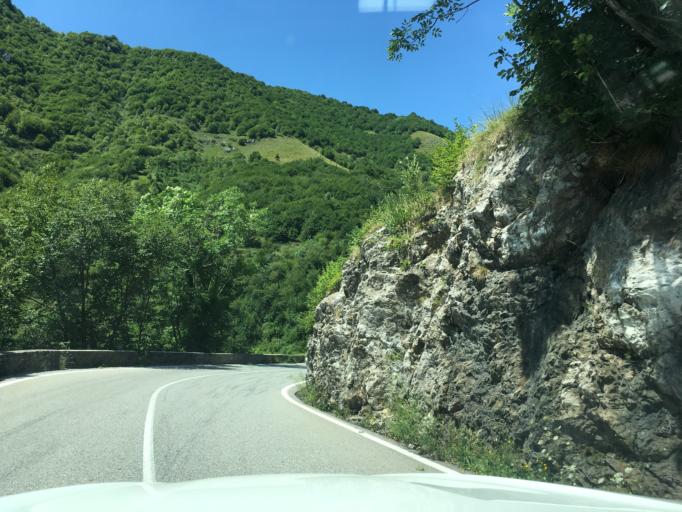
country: IT
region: Lombardy
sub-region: Provincia di Bergamo
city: Selvino
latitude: 45.7704
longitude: 9.7425
